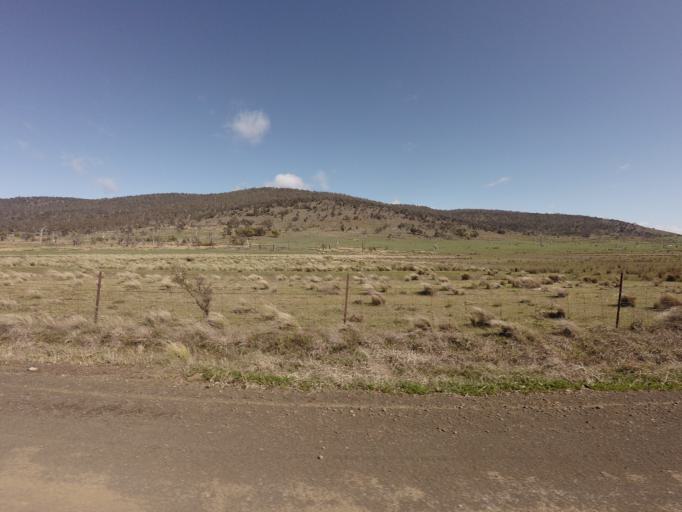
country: AU
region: Tasmania
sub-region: Northern Midlands
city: Evandale
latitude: -41.9298
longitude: 147.4150
